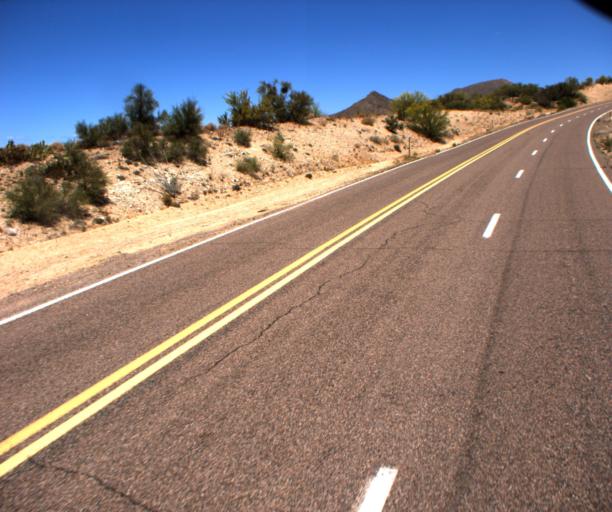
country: US
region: Arizona
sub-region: Yavapai County
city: Bagdad
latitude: 34.4602
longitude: -113.0044
